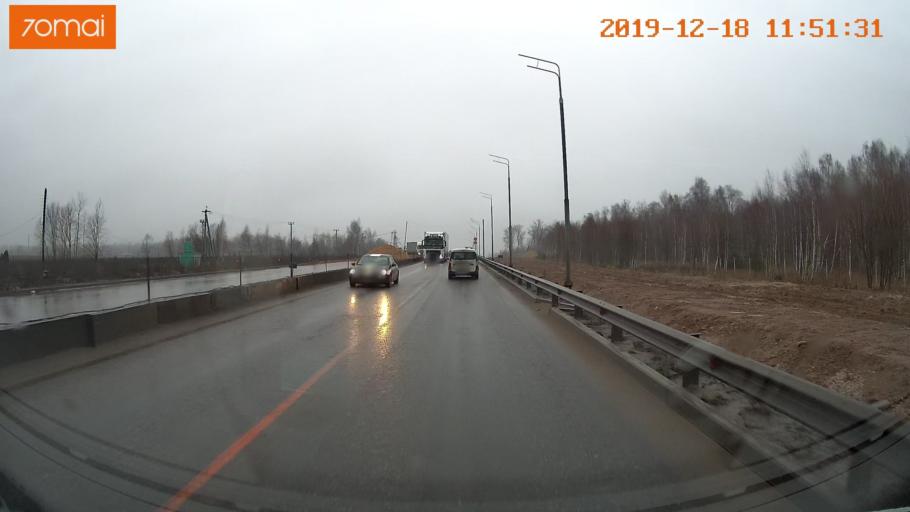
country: RU
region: Moskovskaya
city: Yershovo
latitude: 55.7938
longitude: 36.9219
